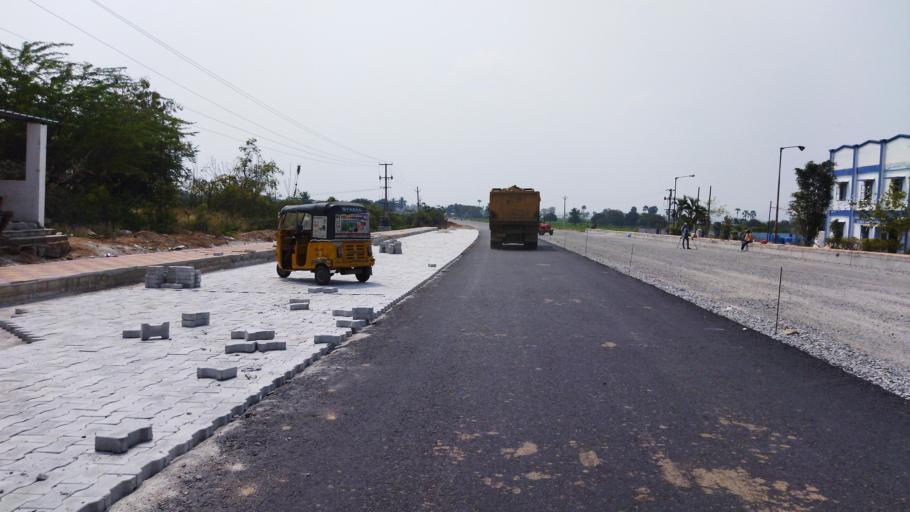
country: IN
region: Telangana
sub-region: Nalgonda
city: Nalgonda
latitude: 17.0893
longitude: 79.3280
